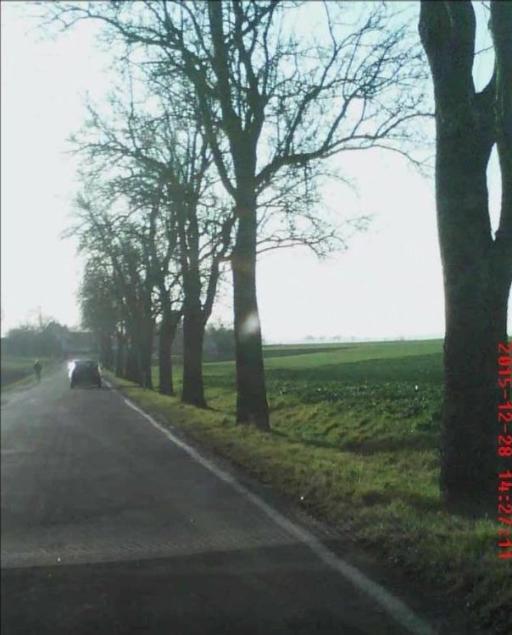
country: DE
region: Thuringia
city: Liebstedt
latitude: 51.0515
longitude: 11.4158
